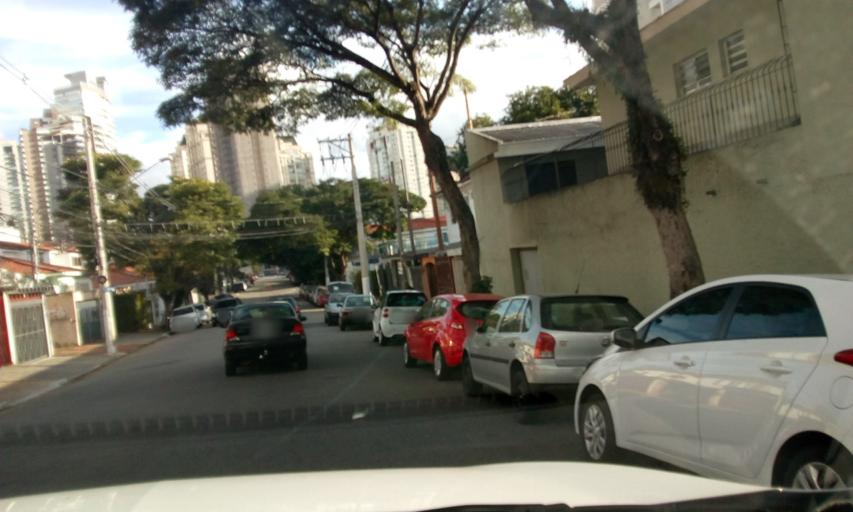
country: BR
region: Sao Paulo
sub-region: Sao Paulo
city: Sao Paulo
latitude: -23.6172
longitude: -46.6940
